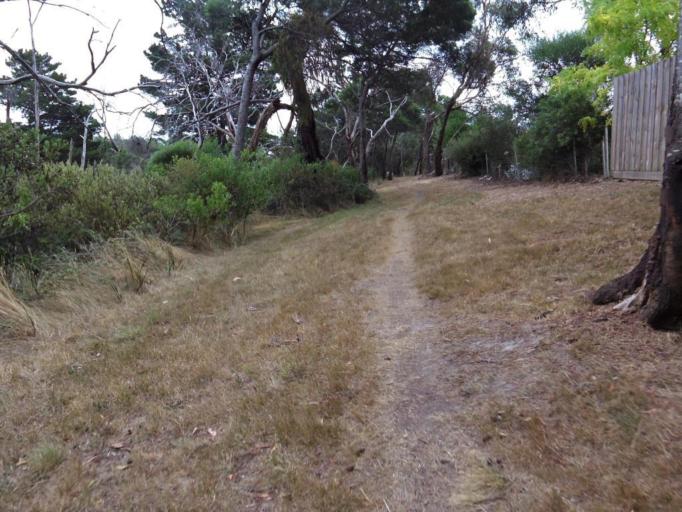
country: AU
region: Victoria
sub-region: Mornington Peninsula
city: Mount Martha
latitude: -38.2887
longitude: 145.0135
